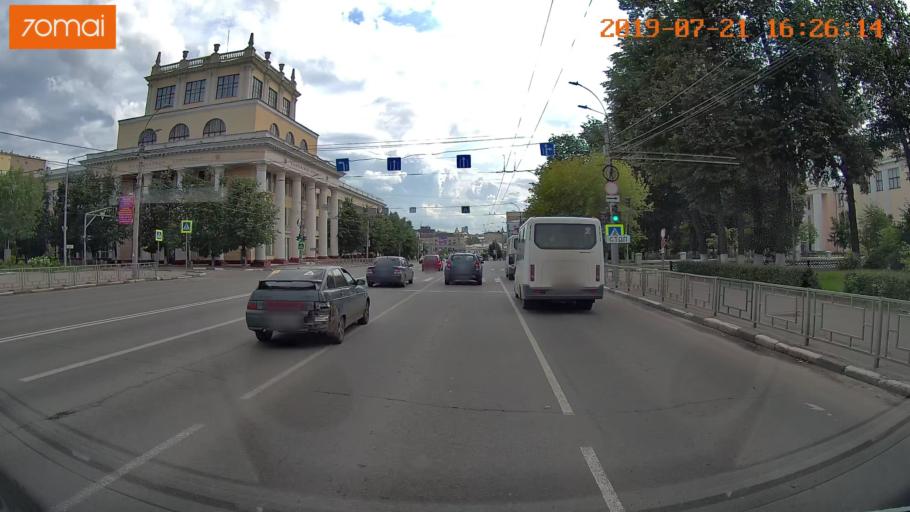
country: RU
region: Ivanovo
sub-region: Gorod Ivanovo
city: Ivanovo
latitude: 56.9988
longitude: 40.9838
